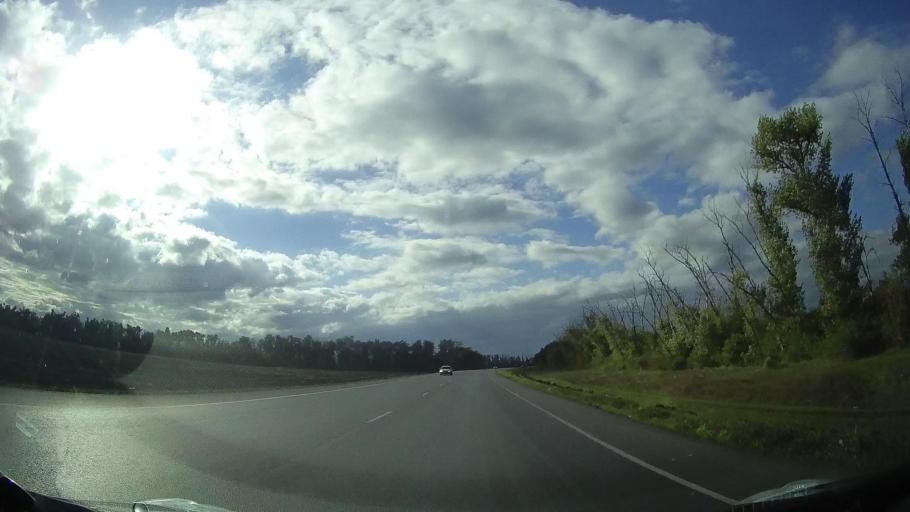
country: RU
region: Rostov
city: Tselina
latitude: 46.5302
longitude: 40.9485
